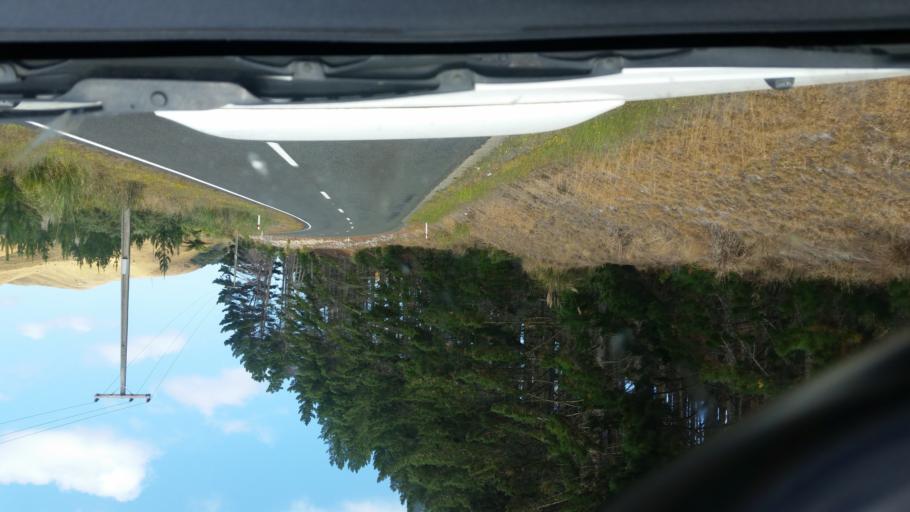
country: NZ
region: Northland
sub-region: Kaipara District
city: Dargaville
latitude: -35.8227
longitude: 173.7030
